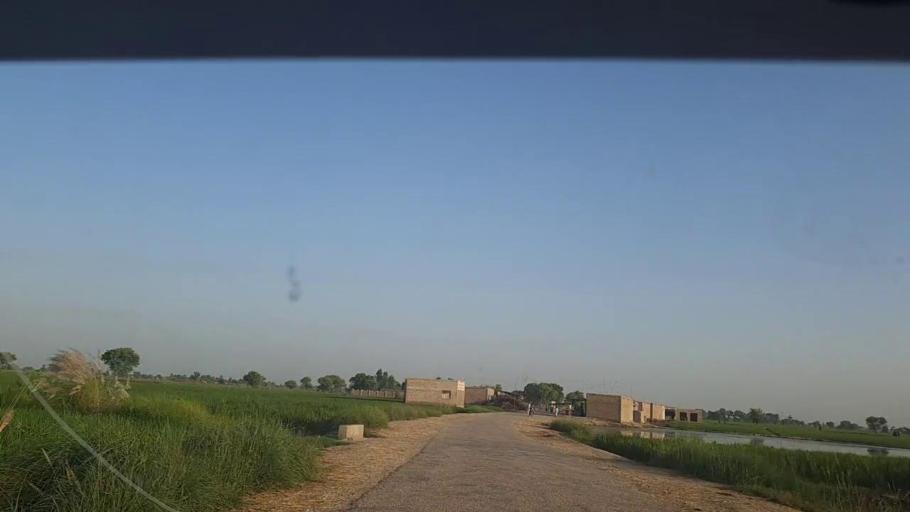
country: PK
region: Sindh
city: Thul
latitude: 28.1314
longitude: 68.8912
